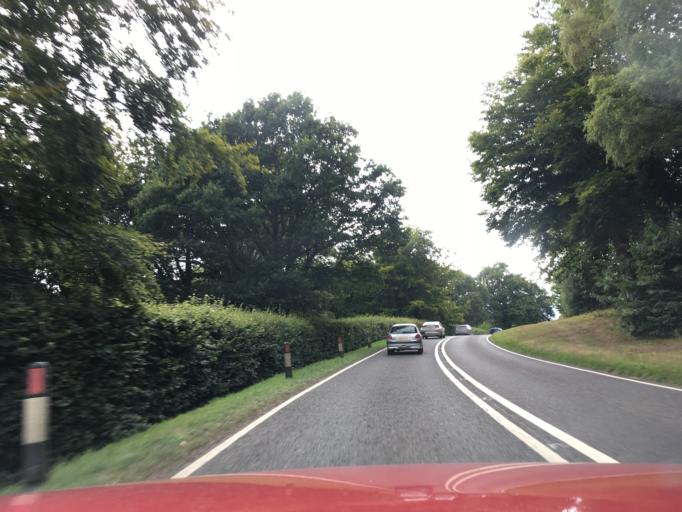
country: GB
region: England
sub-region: West Sussex
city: Midhurst
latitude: 50.9904
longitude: -0.7112
